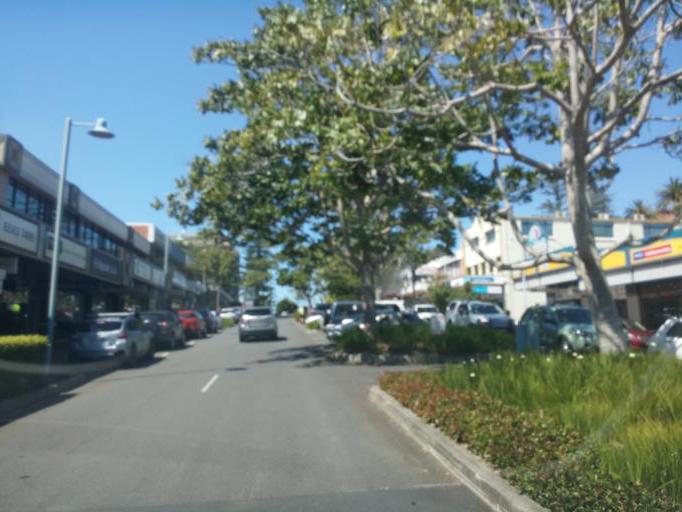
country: AU
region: New South Wales
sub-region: Port Macquarie-Hastings
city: Port Macquarie
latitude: -31.4312
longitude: 152.9084
